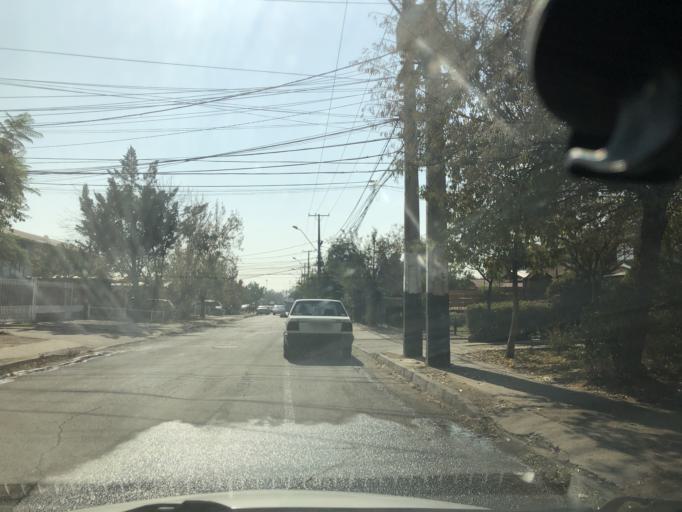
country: CL
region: Santiago Metropolitan
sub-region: Provincia de Cordillera
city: Puente Alto
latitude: -33.5999
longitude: -70.5584
